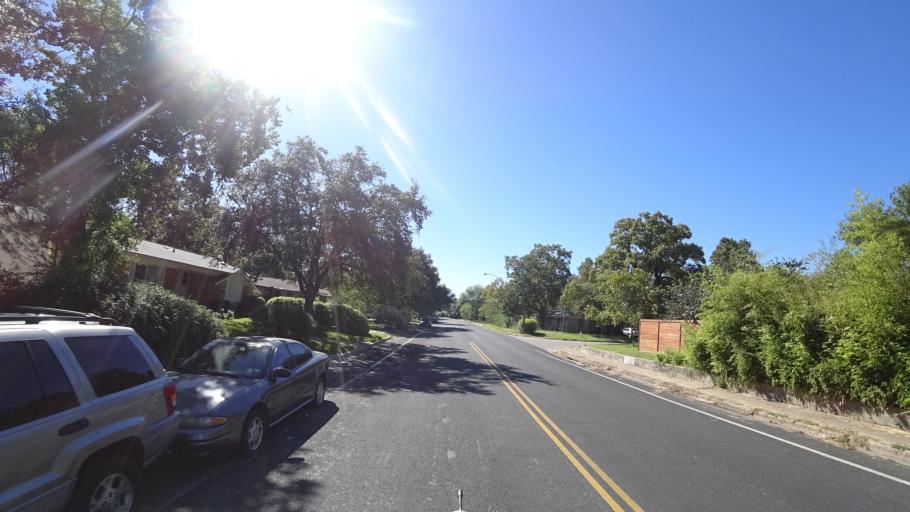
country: US
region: Texas
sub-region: Travis County
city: Austin
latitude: 30.3028
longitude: -97.6865
